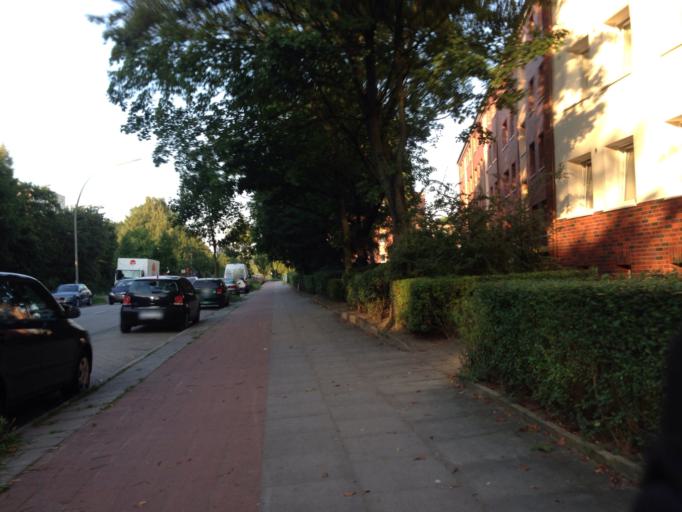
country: DE
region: Schleswig-Holstein
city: Barsbuettel
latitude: 53.5884
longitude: 10.1582
